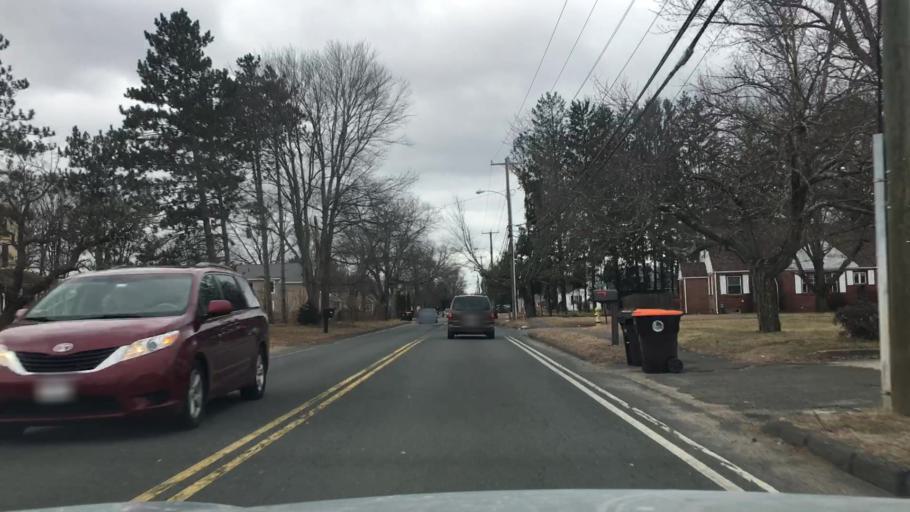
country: US
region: Massachusetts
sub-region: Hampden County
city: Agawam
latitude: 42.0705
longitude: -72.6551
